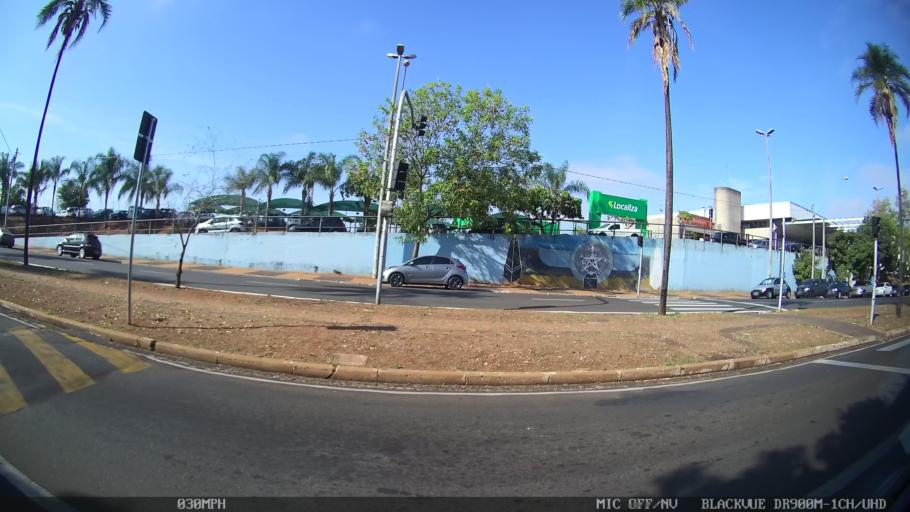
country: BR
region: Sao Paulo
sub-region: Sao Jose Do Rio Preto
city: Sao Jose do Rio Preto
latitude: -20.8114
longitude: -49.4044
